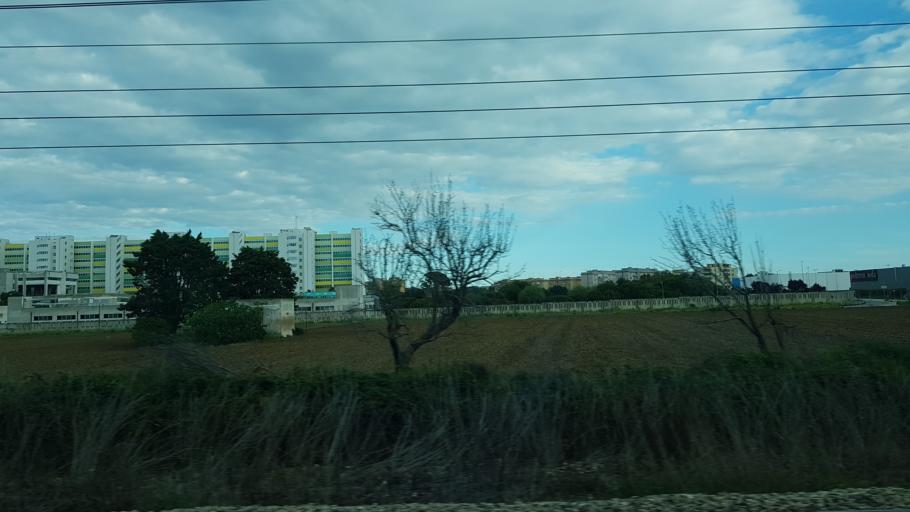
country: IT
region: Apulia
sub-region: Provincia di Brindisi
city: Brindisi
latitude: 40.6257
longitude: 17.9099
